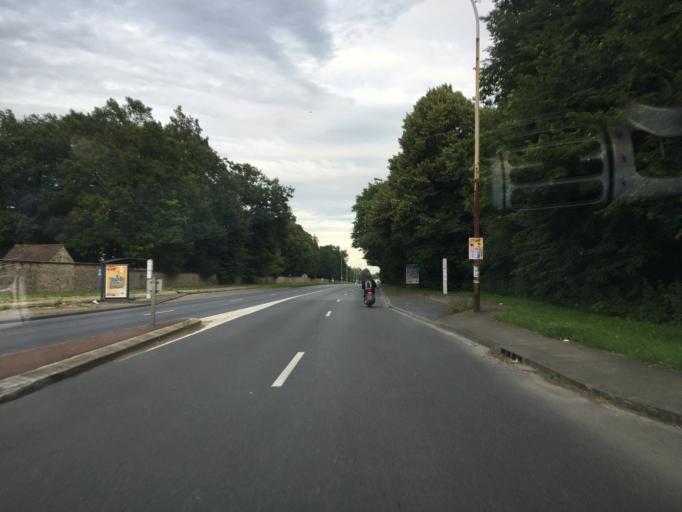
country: FR
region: Ile-de-France
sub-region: Departement du Val-de-Marne
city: Villecresnes
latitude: 48.7313
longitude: 2.5238
